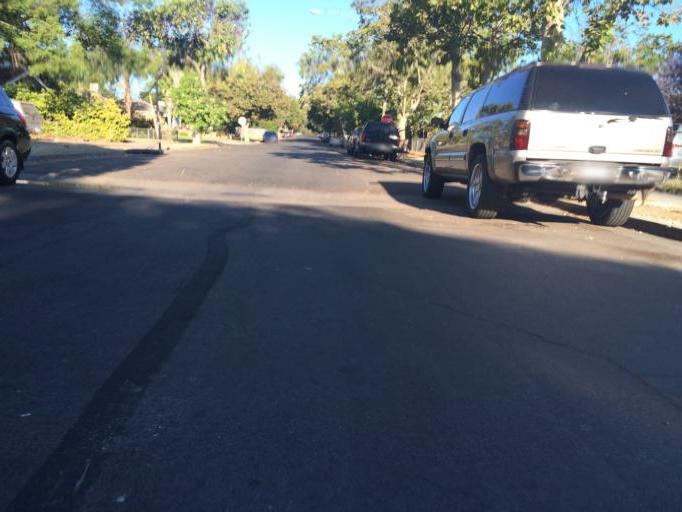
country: US
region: California
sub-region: Fresno County
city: Fresno
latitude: 36.7495
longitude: -119.7599
